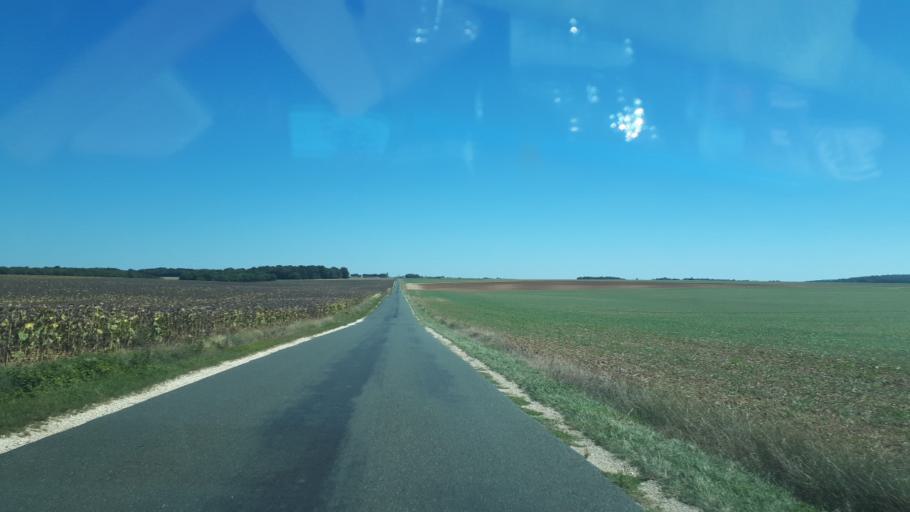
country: FR
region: Centre
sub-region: Departement du Cher
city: Rians
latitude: 47.1856
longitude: 2.6504
